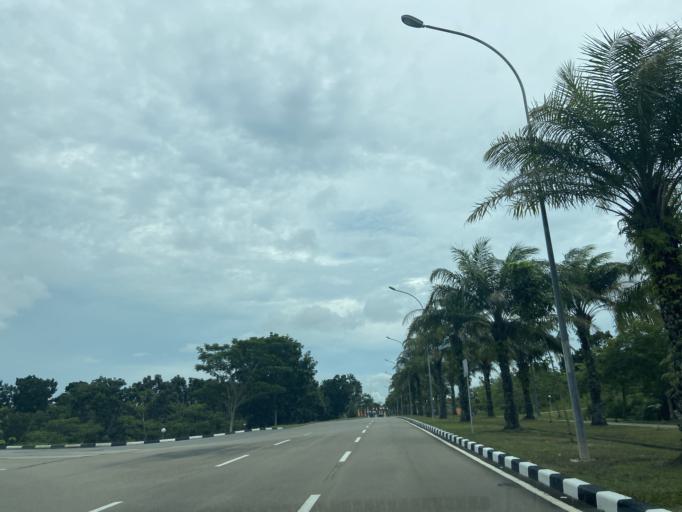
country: SG
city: Singapore
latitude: 1.1250
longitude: 104.1141
